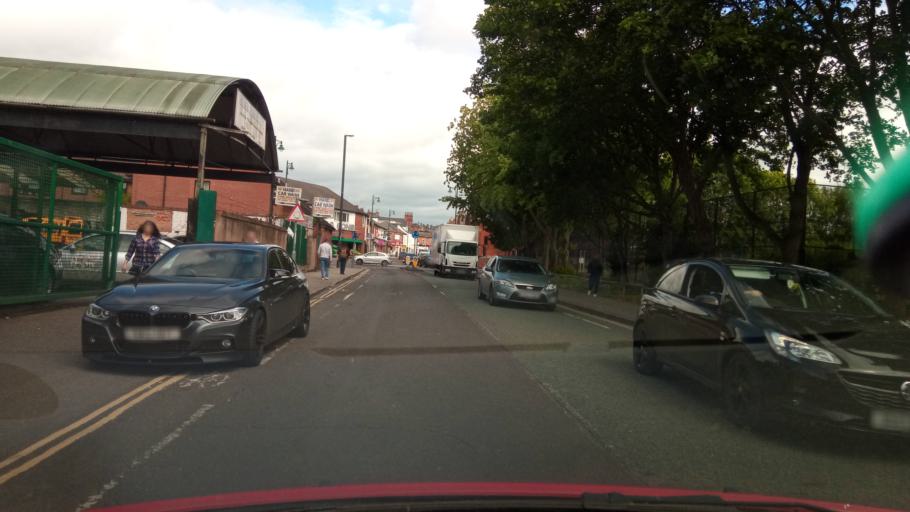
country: GB
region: England
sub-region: Derby
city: Derby
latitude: 52.9071
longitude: -1.4781
